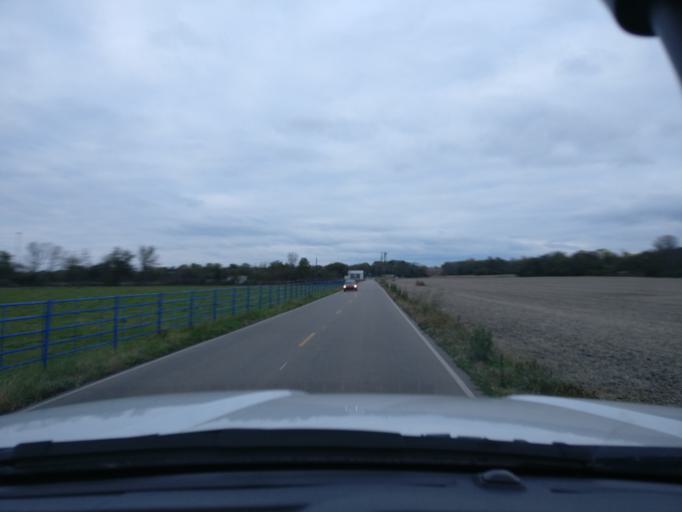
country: US
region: Ohio
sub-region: Warren County
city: Hunter
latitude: 39.4601
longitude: -84.3204
